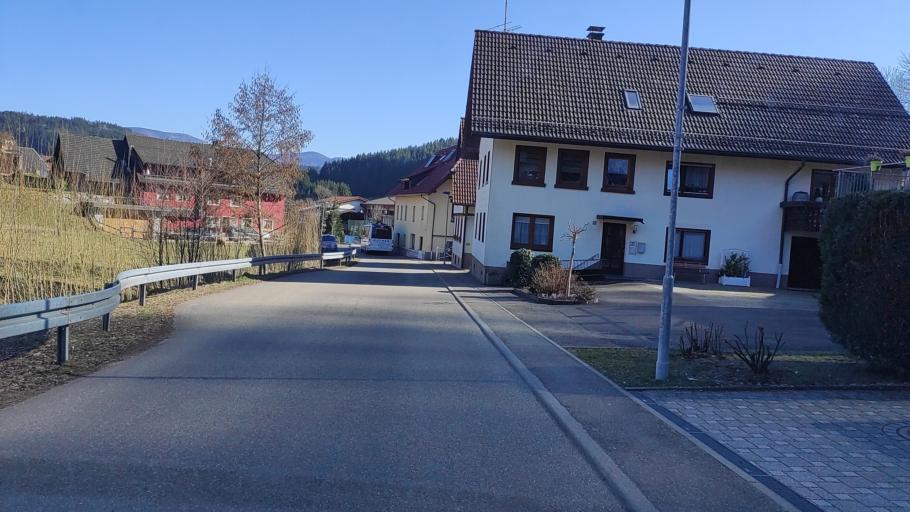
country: DE
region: Baden-Wuerttemberg
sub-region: Freiburg Region
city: Elzach
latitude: 48.1942
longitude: 8.0320
